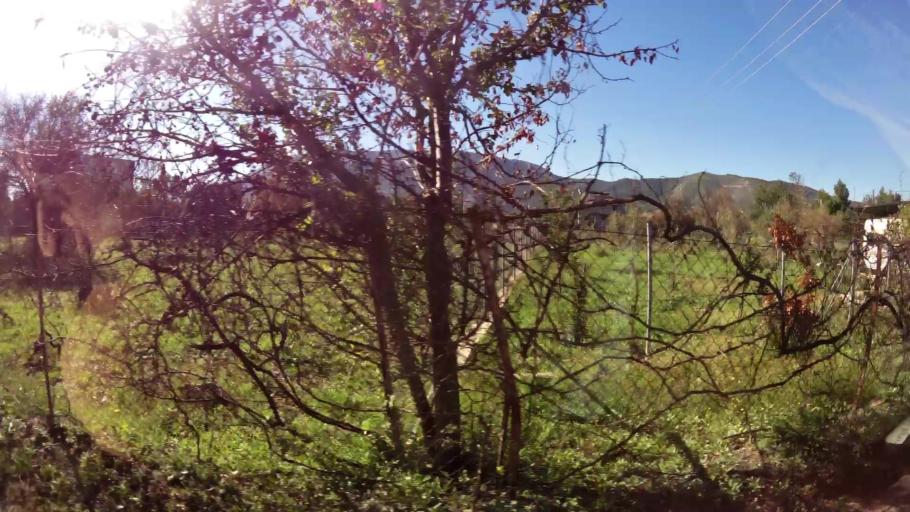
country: GR
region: Attica
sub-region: Nomarchia Anatolikis Attikis
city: Paiania
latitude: 37.9680
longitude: 23.8626
